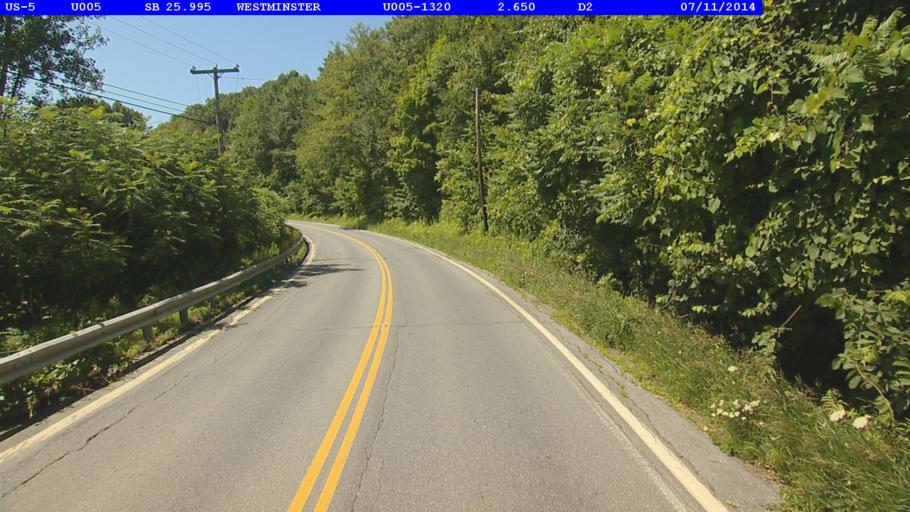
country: US
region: Vermont
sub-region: Windham County
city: Bellows Falls
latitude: 43.0570
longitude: -72.4691
